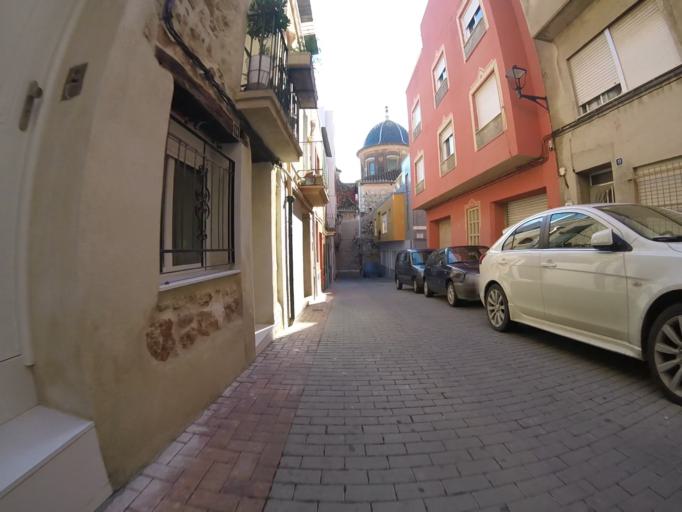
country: ES
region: Valencia
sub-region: Provincia de Castello
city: Torreblanca
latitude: 40.2213
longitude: 0.1958
